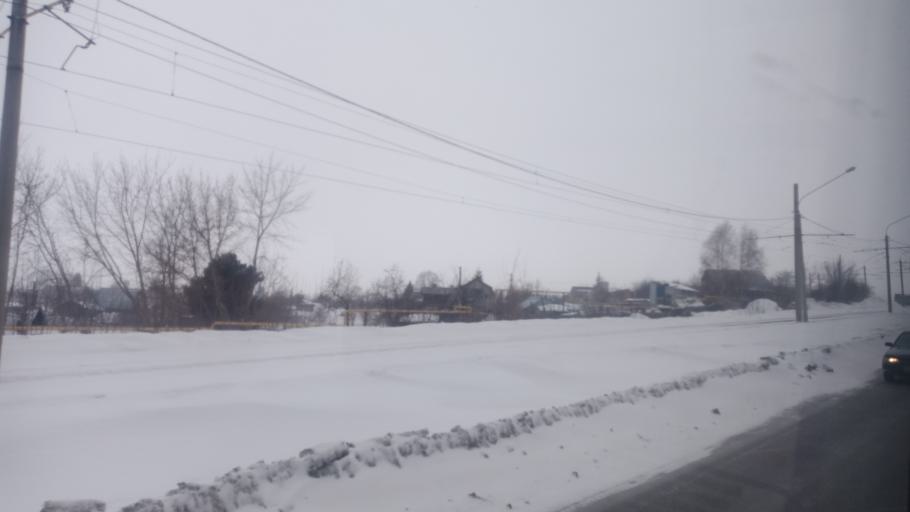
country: RU
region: Altai Krai
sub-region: Gorod Barnaulskiy
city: Barnaul
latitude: 53.3891
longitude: 83.6784
